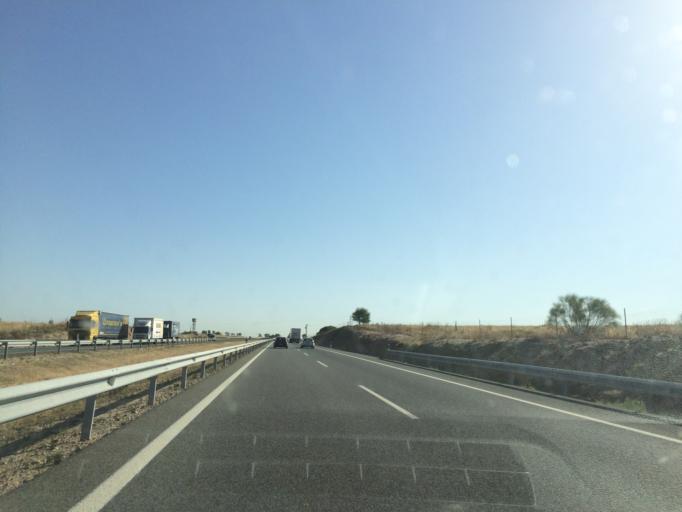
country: ES
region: Castille-La Mancha
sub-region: Province of Toledo
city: Santa Cruz del Retamar
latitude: 40.1212
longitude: -4.2577
